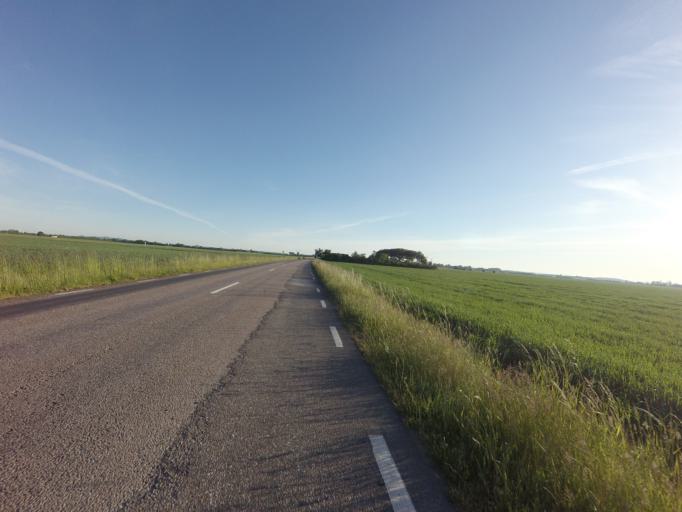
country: SE
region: Skane
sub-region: Helsingborg
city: Odakra
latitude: 56.1819
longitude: 12.6765
